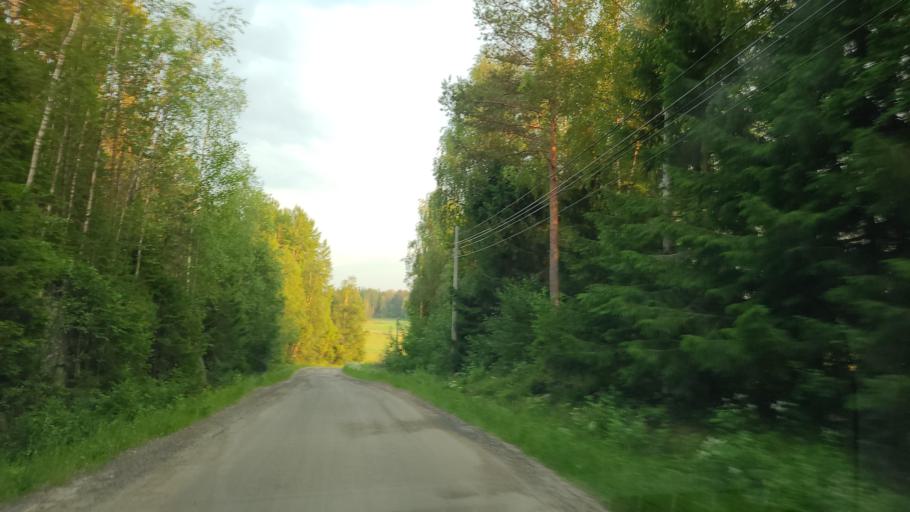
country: SE
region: Vaesterbotten
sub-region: Robertsfors Kommun
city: Robertsfors
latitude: 64.0671
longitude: 20.8715
